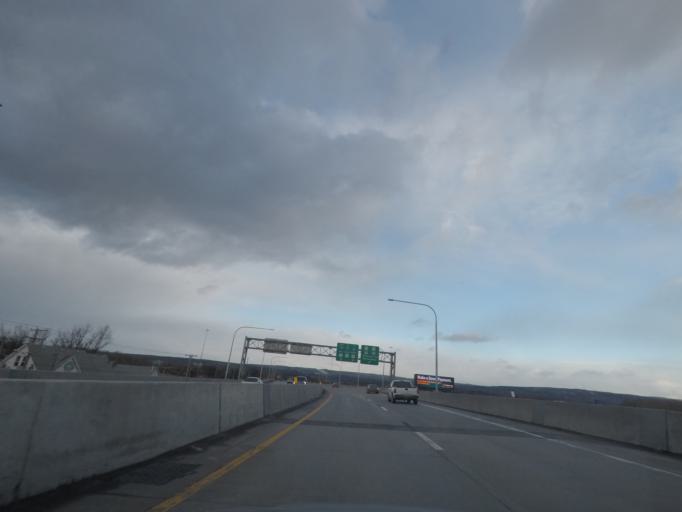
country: US
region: New York
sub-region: Oneida County
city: Utica
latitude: 43.1037
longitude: -75.2395
